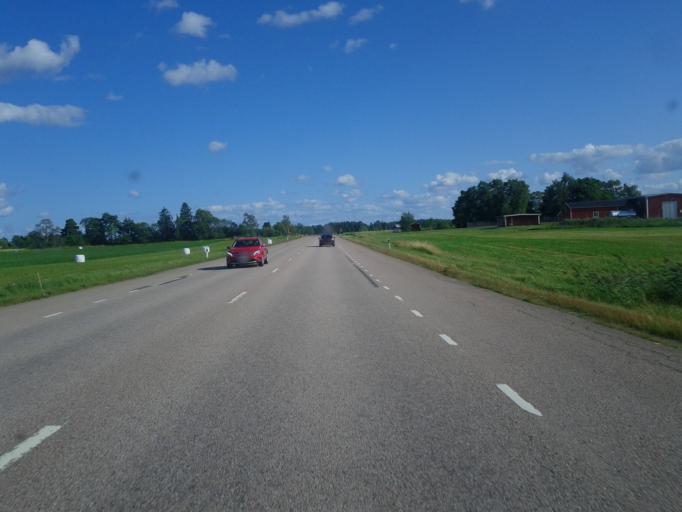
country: SE
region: Uppsala
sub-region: Enkopings Kommun
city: Enkoping
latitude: 59.6879
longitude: 17.0342
